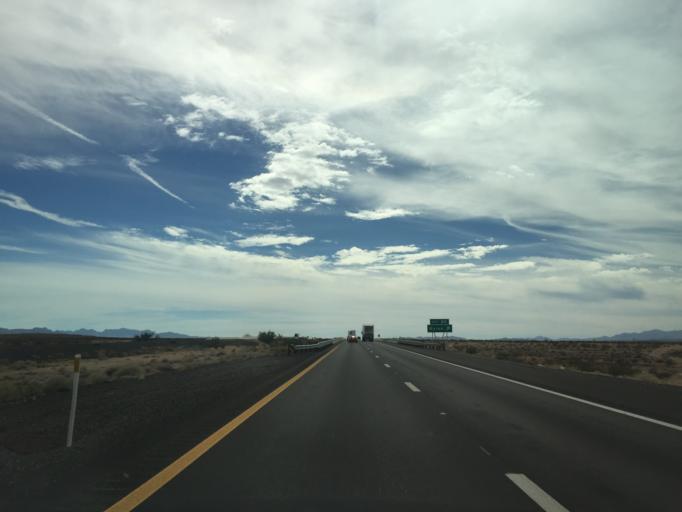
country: US
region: Nevada
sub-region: Clark County
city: Moapa Town
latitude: 36.5933
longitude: -114.6457
